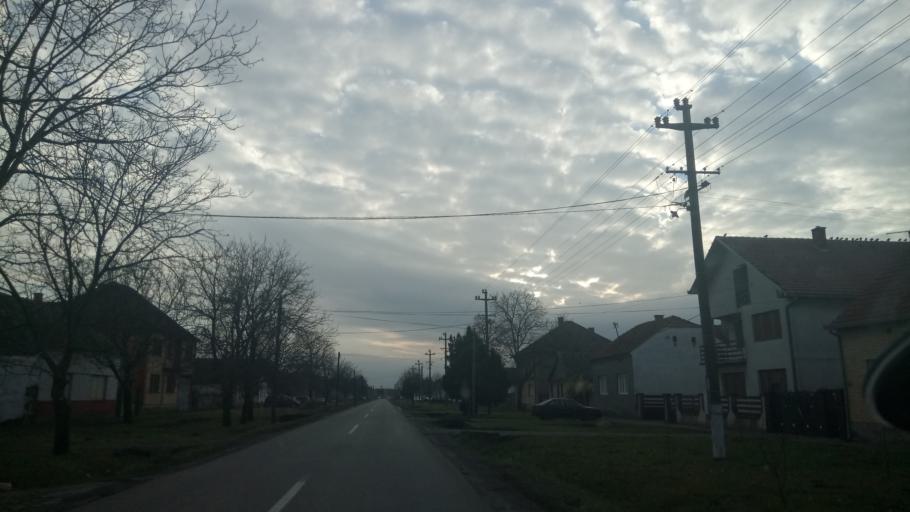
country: RS
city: Vojka
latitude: 44.9403
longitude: 20.1697
